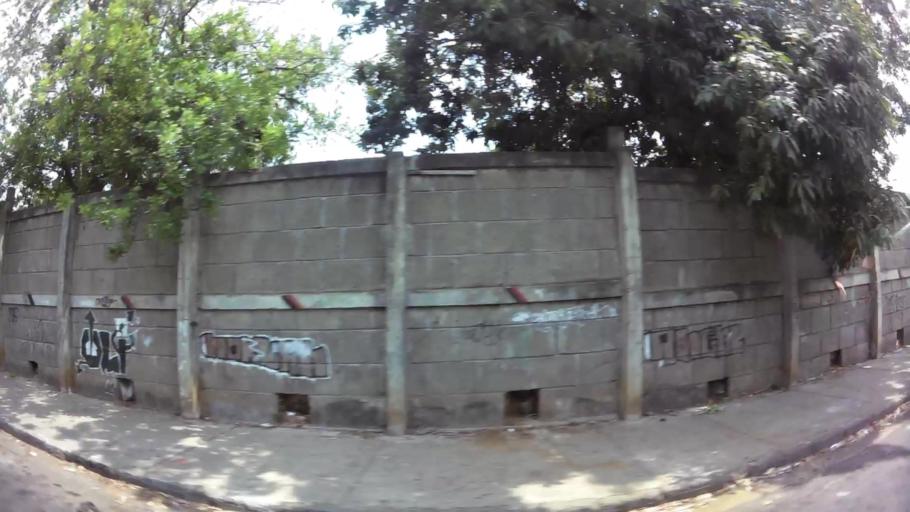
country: NI
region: Managua
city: Managua
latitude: 12.1532
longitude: -86.2924
